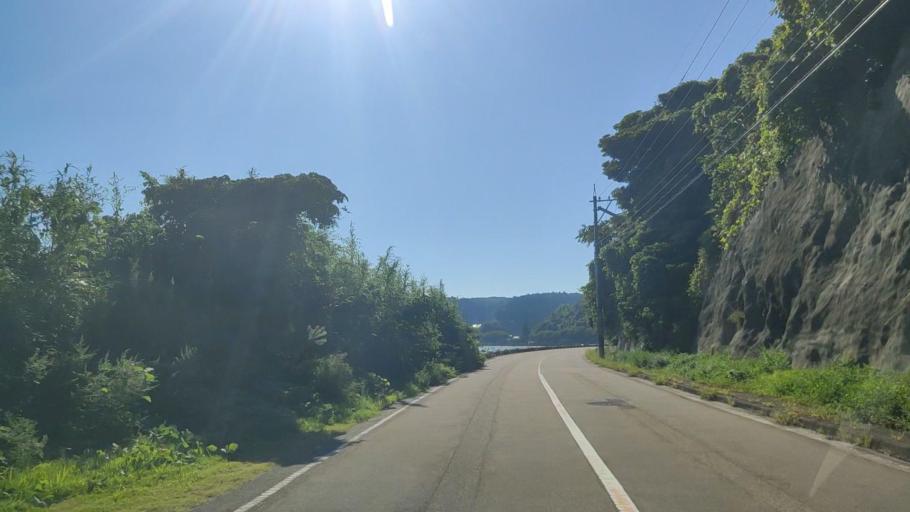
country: JP
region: Ishikawa
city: Nanao
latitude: 37.2798
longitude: 137.1045
